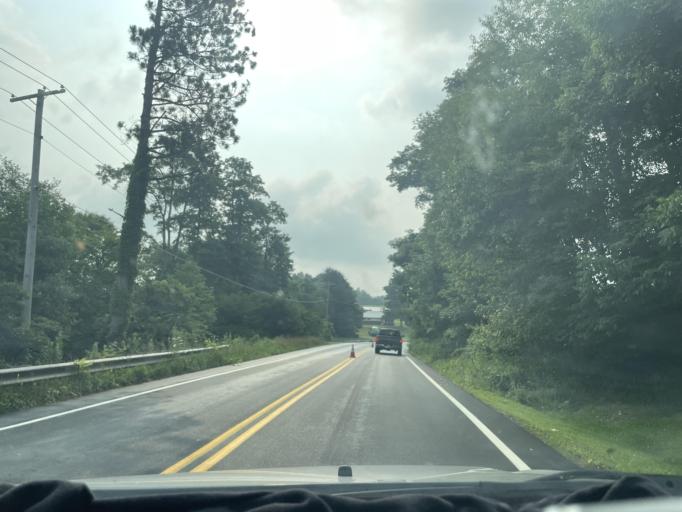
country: US
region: Maryland
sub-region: Garrett County
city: Mountain Lake Park
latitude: 39.2927
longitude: -79.3565
